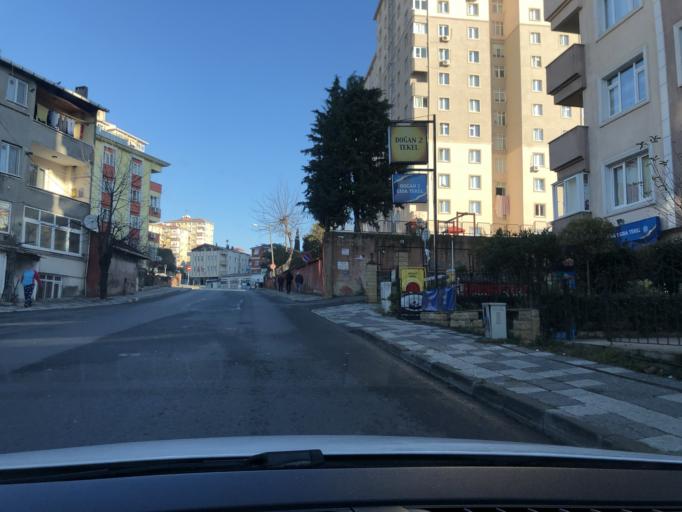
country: TR
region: Istanbul
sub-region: Atasehir
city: Atasehir
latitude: 40.9695
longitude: 29.1198
